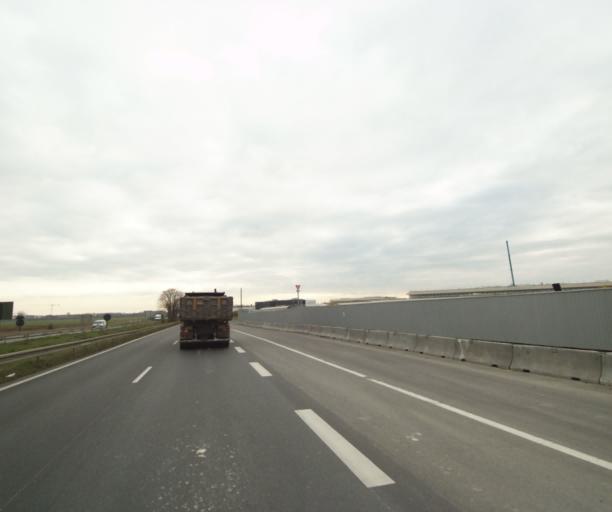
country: FR
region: Ile-de-France
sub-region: Departement du Val-d'Oise
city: Gonesse
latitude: 48.9726
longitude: 2.4617
